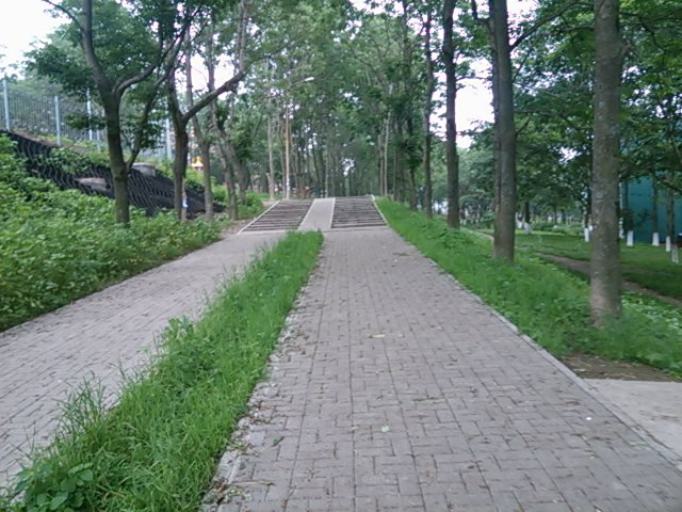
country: RU
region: Primorskiy
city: Vladivostok
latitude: 43.0944
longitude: 131.9675
